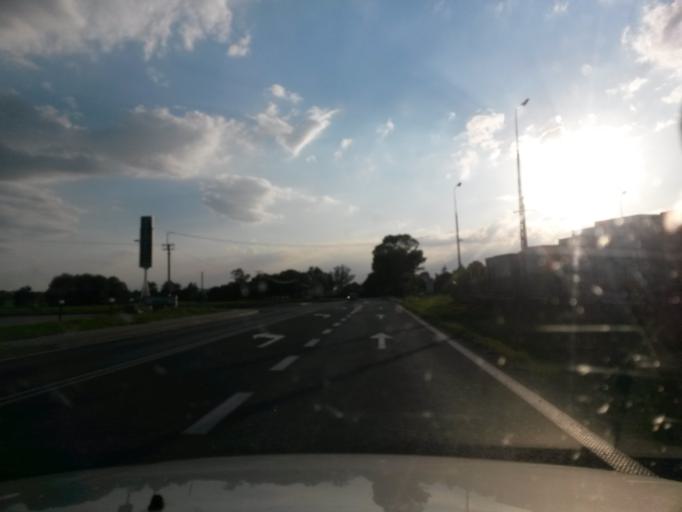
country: PL
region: Lodz Voivodeship
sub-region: Powiat wielunski
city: Wielun
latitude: 51.2297
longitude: 18.6080
